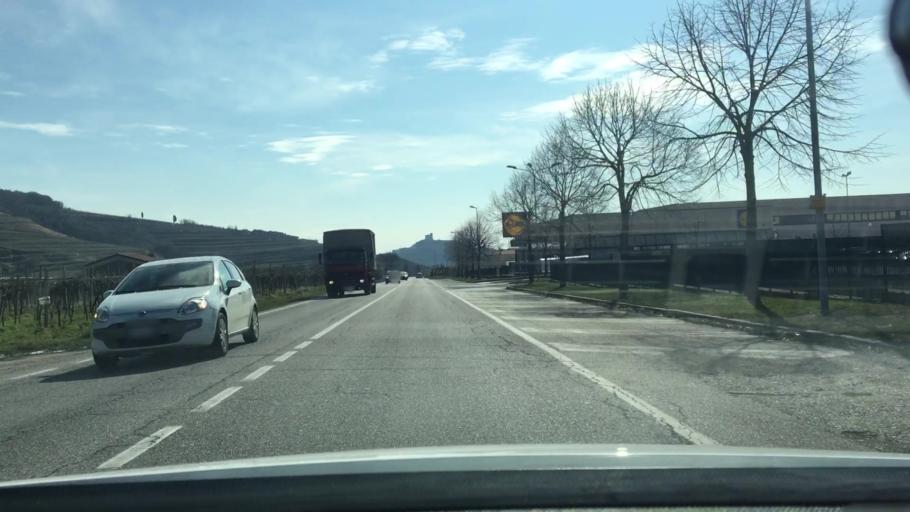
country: IT
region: Veneto
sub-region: Provincia di Verona
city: Cellore
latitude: 45.4998
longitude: 11.1708
